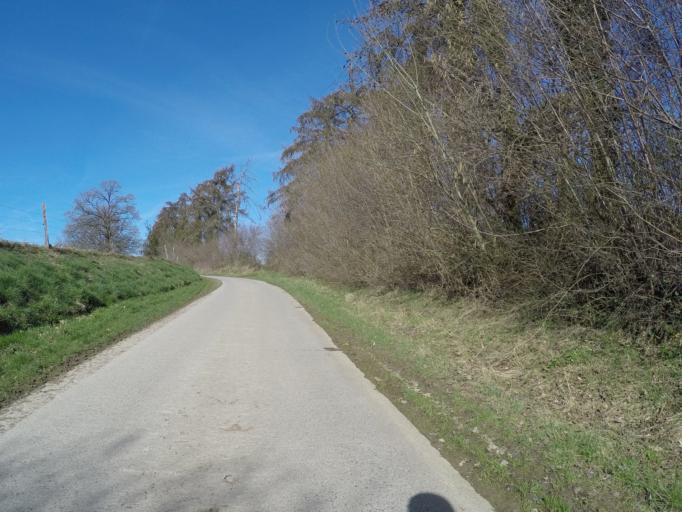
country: BE
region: Wallonia
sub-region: Province de Namur
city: Hamois
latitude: 50.3516
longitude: 5.1135
